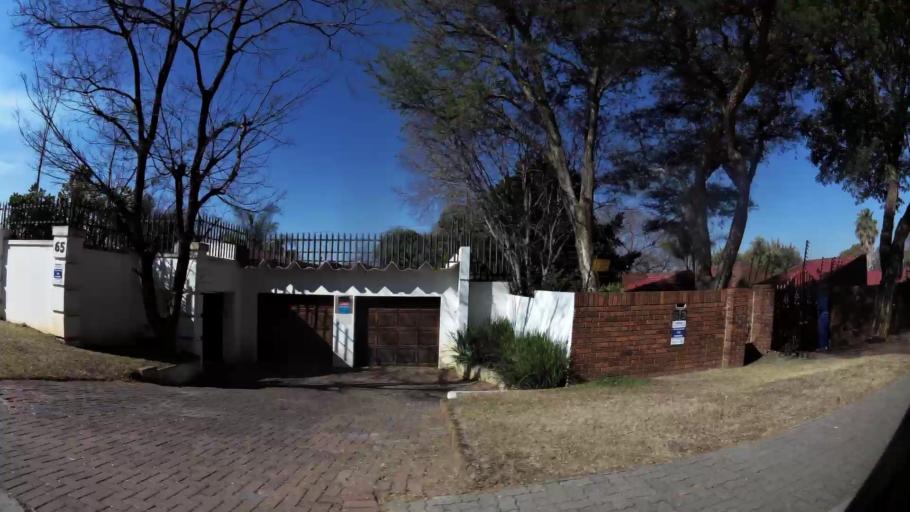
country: ZA
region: Gauteng
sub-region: City of Johannesburg Metropolitan Municipality
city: Roodepoort
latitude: -26.1099
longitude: 27.9608
